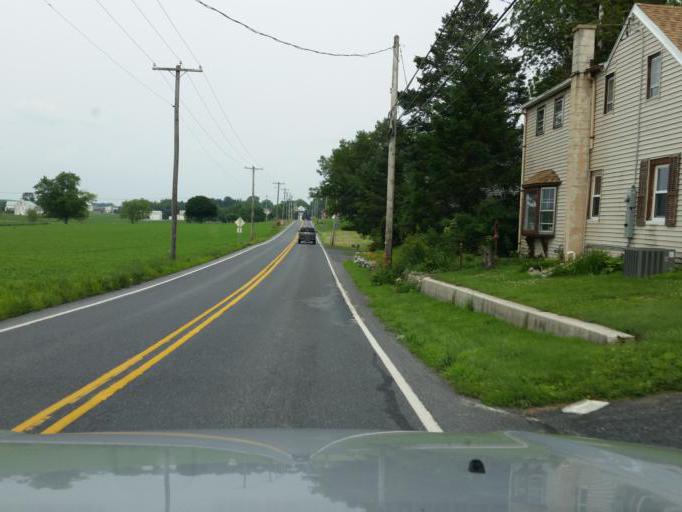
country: US
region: Pennsylvania
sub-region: Lancaster County
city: Lititz
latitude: 40.1534
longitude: -76.3368
